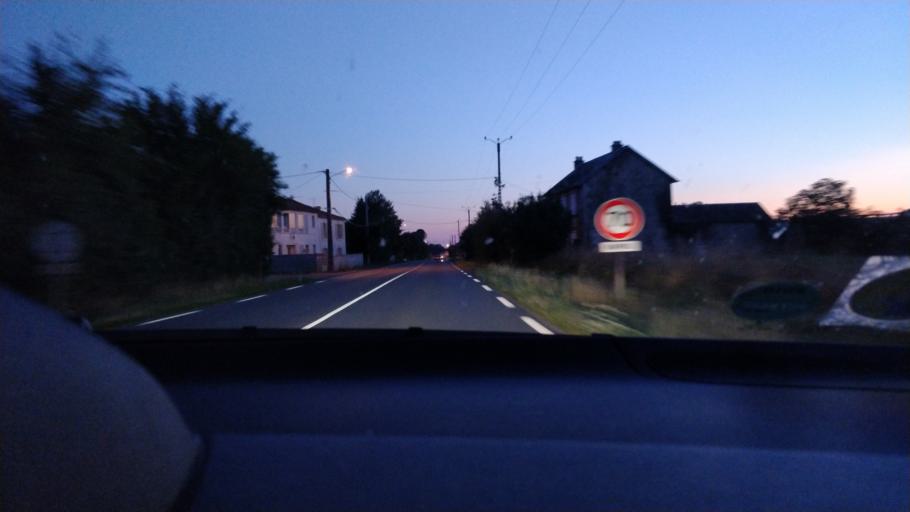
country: FR
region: Poitou-Charentes
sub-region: Departement de la Charente
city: Saint-Claud
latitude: 45.8511
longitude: 0.5039
